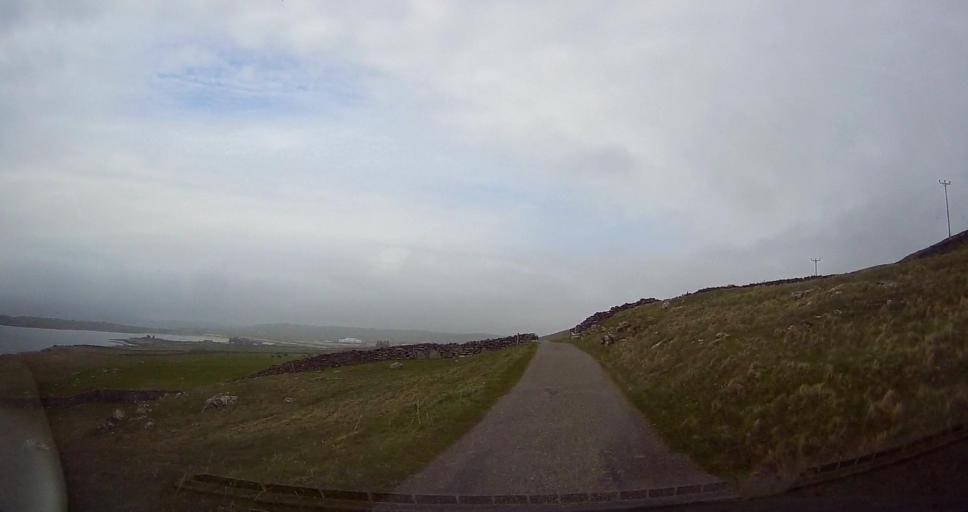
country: GB
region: Scotland
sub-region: Shetland Islands
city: Sandwick
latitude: 59.8606
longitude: -1.2783
